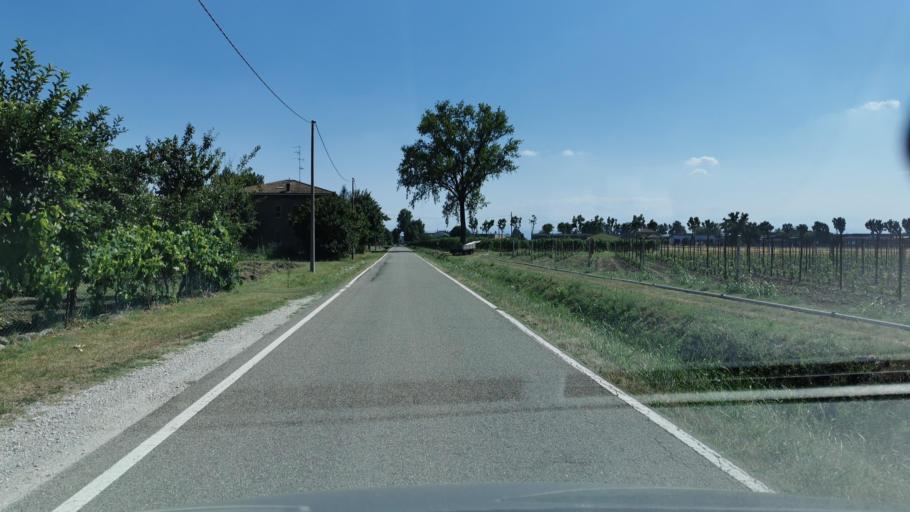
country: IT
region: Emilia-Romagna
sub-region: Provincia di Modena
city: Limidi
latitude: 44.7704
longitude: 10.9171
